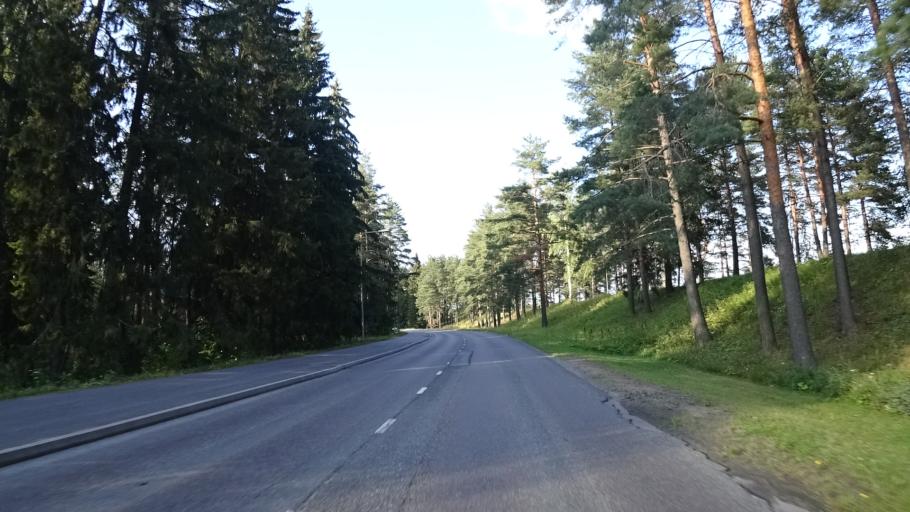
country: FI
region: South Karelia
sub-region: Imatra
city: Imatra
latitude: 61.1784
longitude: 28.7808
